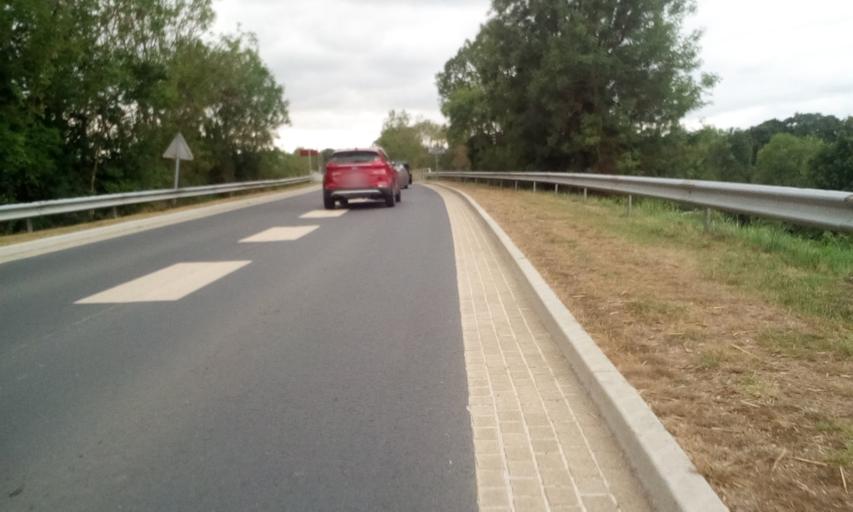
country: FR
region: Lower Normandy
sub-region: Departement du Calvados
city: Troarn
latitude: 49.1882
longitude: -0.1905
